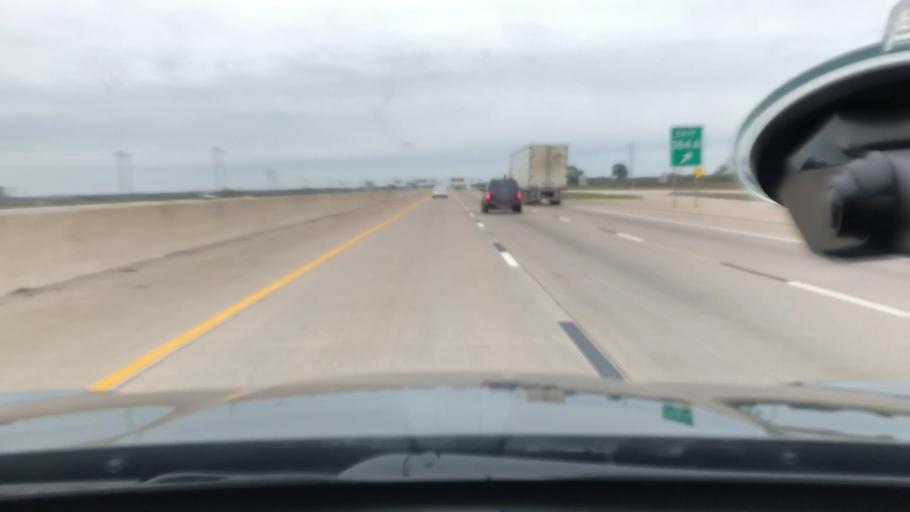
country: US
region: Texas
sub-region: Hill County
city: Hillsboro
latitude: 31.9429
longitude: -97.1092
